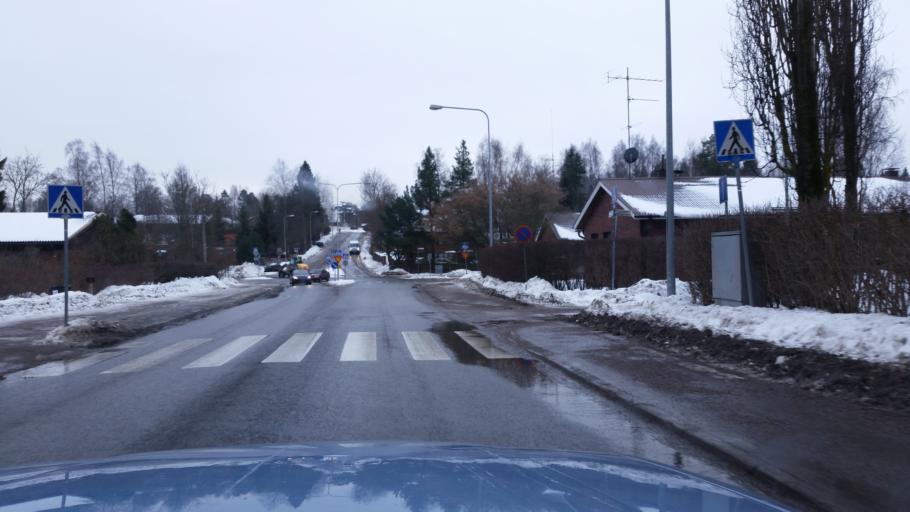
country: FI
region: Uusimaa
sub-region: Helsinki
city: Vantaa
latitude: 60.2722
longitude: 25.0450
